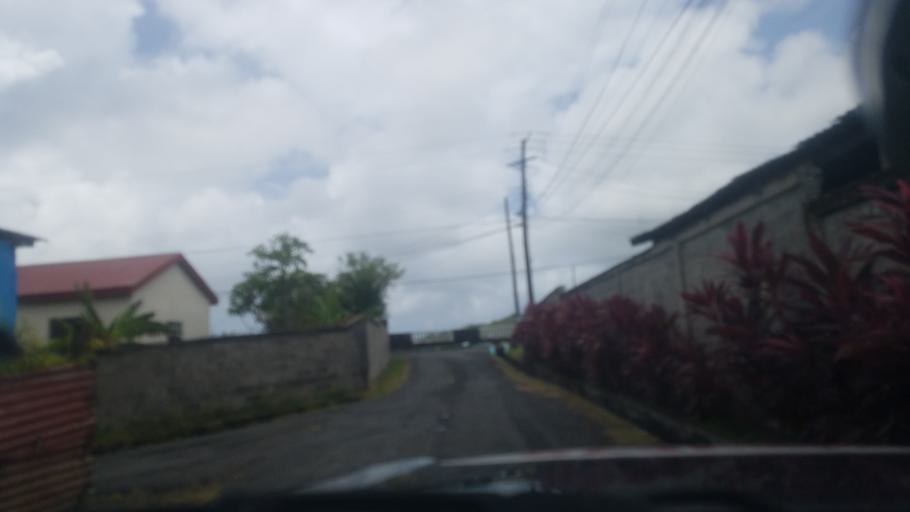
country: LC
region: Vieux-Fort
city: Vieux Fort
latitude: 13.7387
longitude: -60.9571
